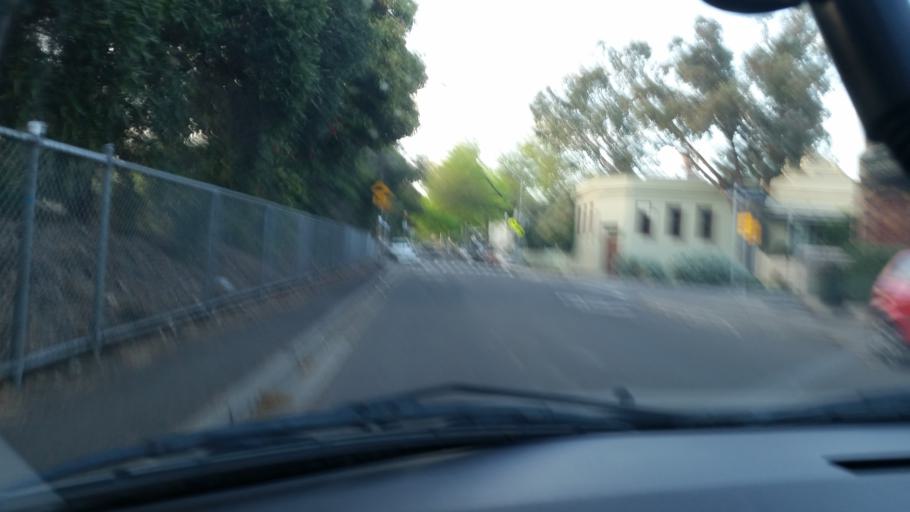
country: AU
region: Victoria
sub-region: Moonee Valley
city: Flemington
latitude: -37.7859
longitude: 144.9288
